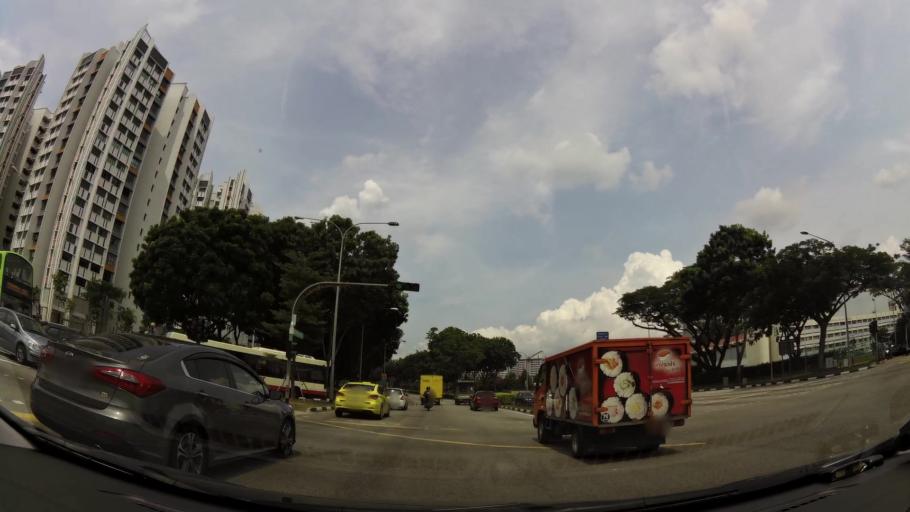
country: MY
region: Johor
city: Johor Bahru
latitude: 1.3404
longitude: 103.7093
